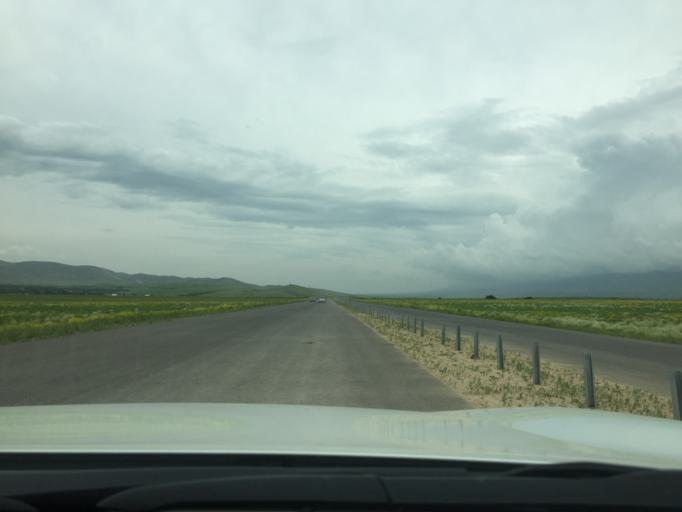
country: KZ
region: Ongtustik Qazaqstan
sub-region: Tulkibas Audany
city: Zhabagly
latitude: 42.5080
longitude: 70.4789
